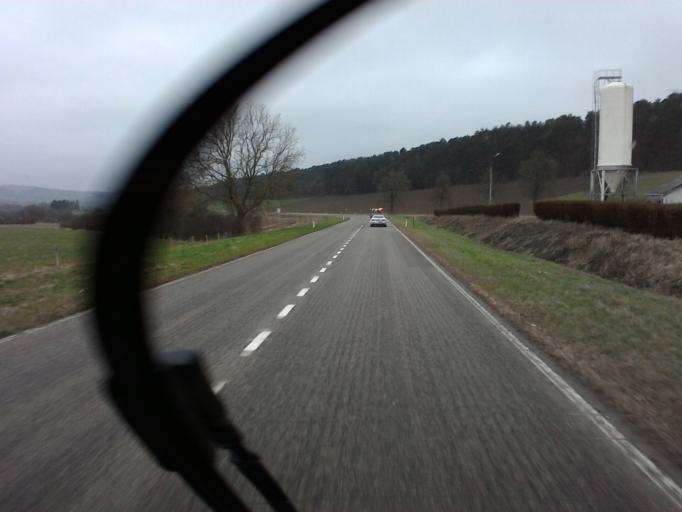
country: BE
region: Wallonia
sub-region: Province du Luxembourg
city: Wellin
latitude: 50.0819
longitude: 5.0879
